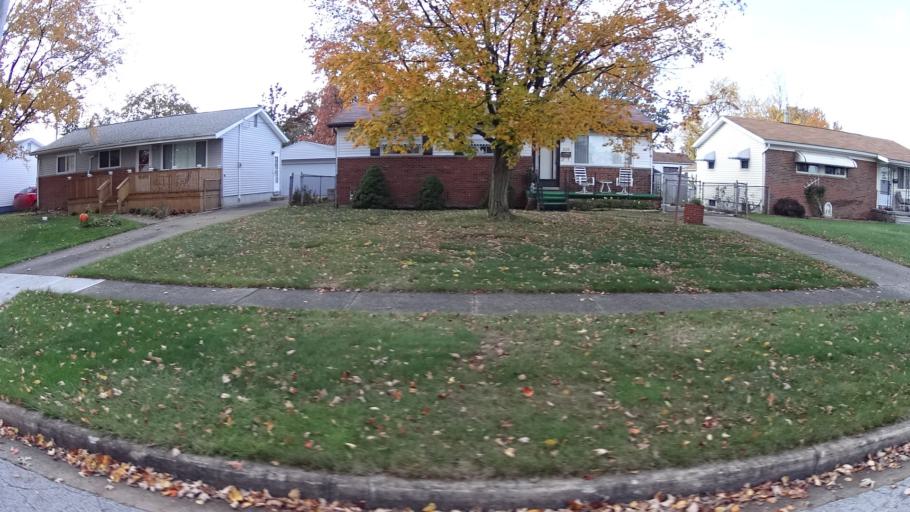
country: US
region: Ohio
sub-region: Lorain County
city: Sheffield
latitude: 41.4268
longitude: -82.1131
